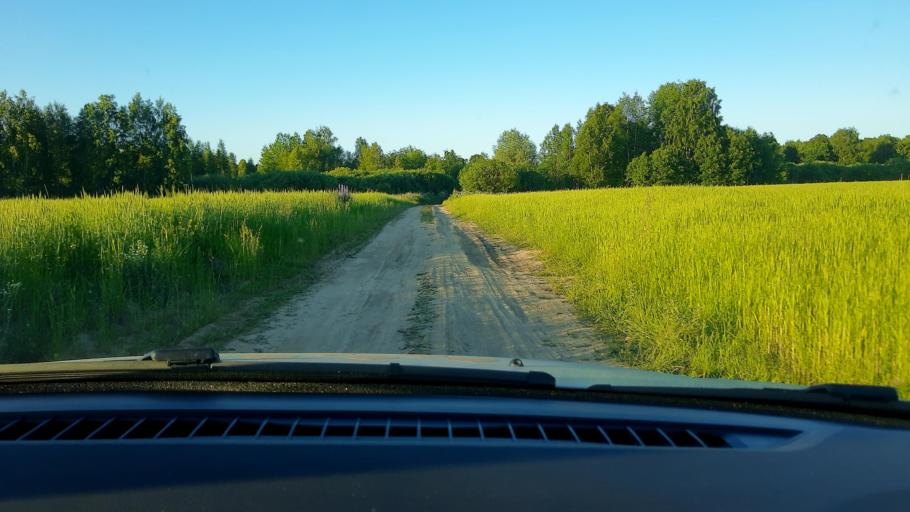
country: RU
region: Nizjnij Novgorod
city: Kstovo
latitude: 56.3077
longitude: 44.2678
